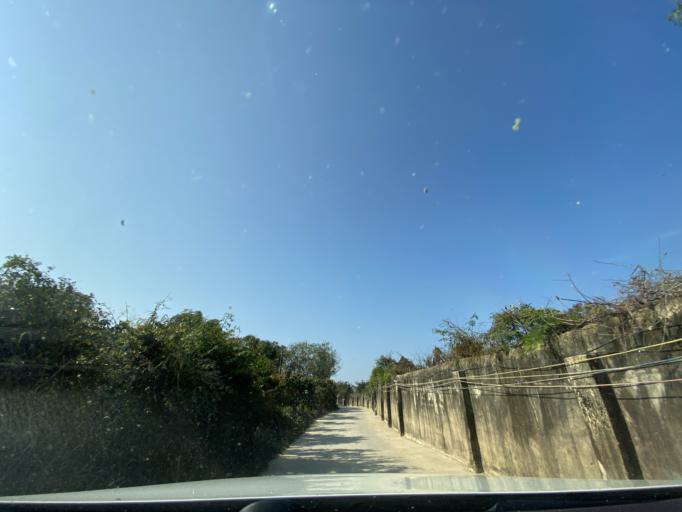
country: CN
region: Hainan
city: Haitangwan
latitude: 18.3987
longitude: 109.7681
